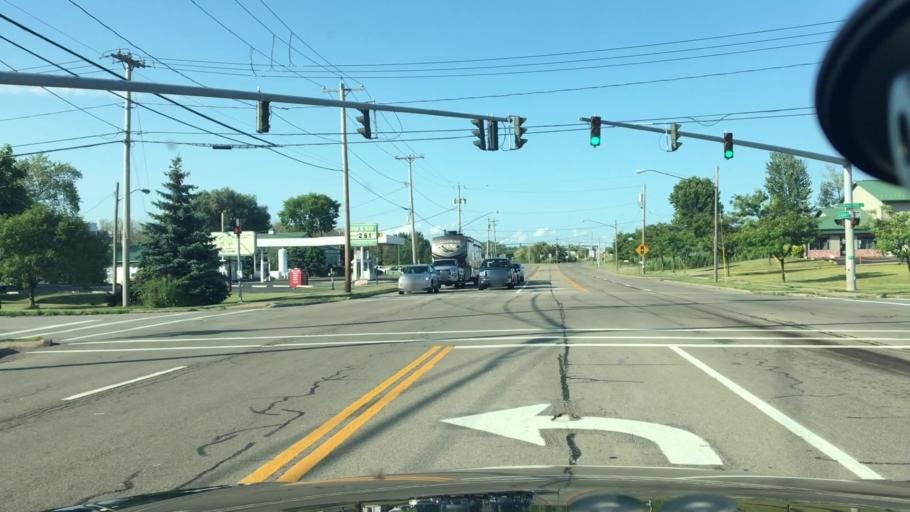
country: US
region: New York
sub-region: Erie County
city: Blasdell
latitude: 42.7722
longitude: -78.8610
